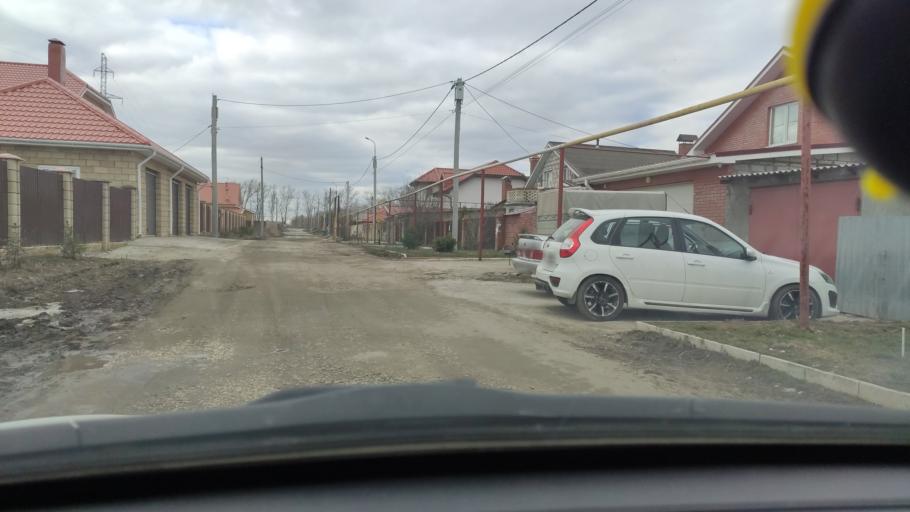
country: RU
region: Samara
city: Tol'yatti
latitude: 53.5500
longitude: 49.3983
